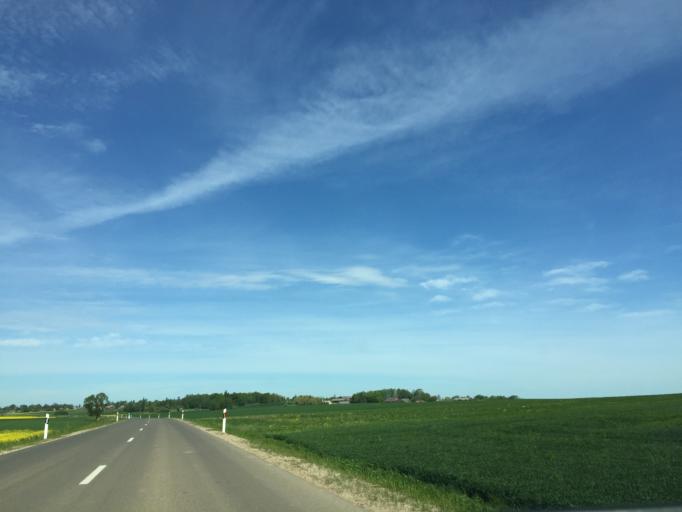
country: LT
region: Panevezys
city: Pasvalys
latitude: 56.1107
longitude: 24.2437
